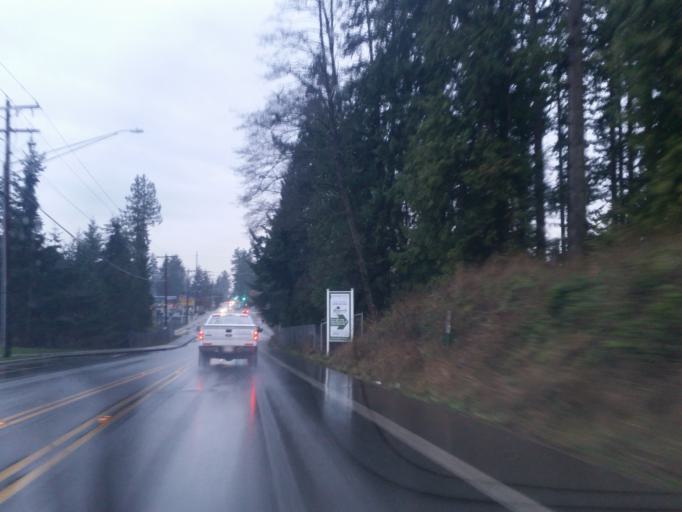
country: US
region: Washington
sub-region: Snohomish County
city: Meadowdale
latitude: 47.8493
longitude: -122.3037
